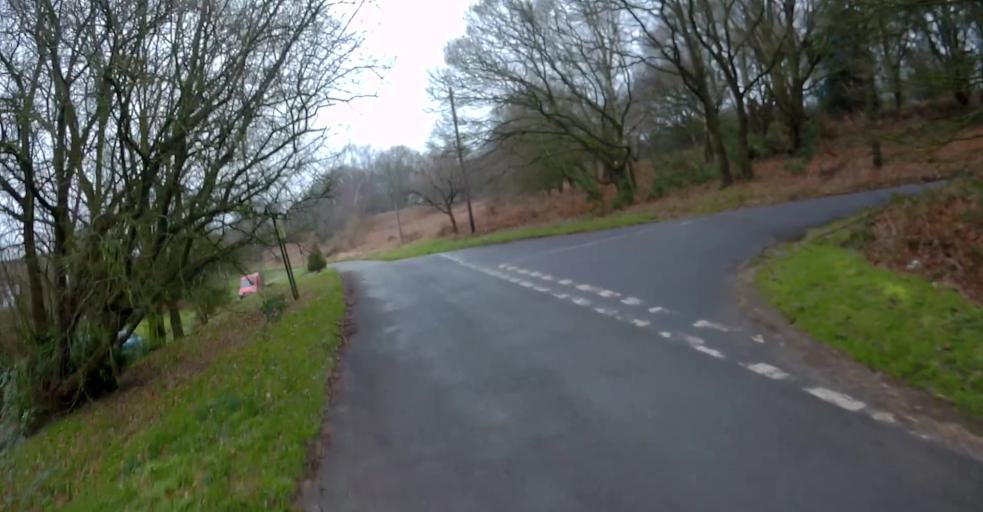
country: GB
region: England
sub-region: Hampshire
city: Hook
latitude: 51.3243
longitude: -0.9340
